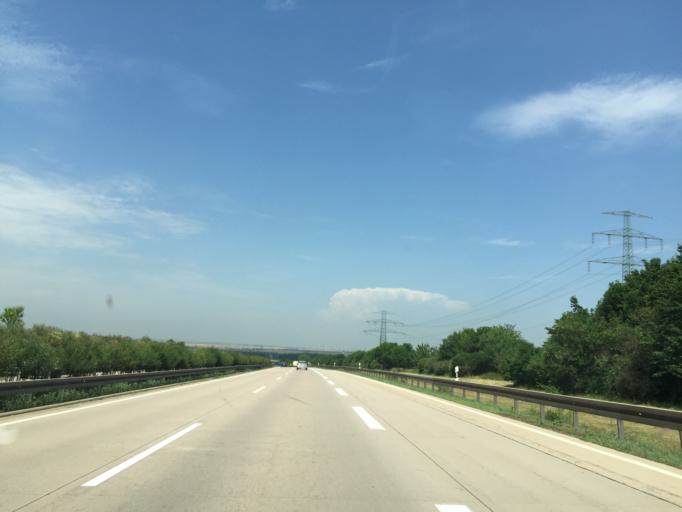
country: DE
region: Thuringia
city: Alkersleben
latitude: 50.8546
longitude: 11.0080
